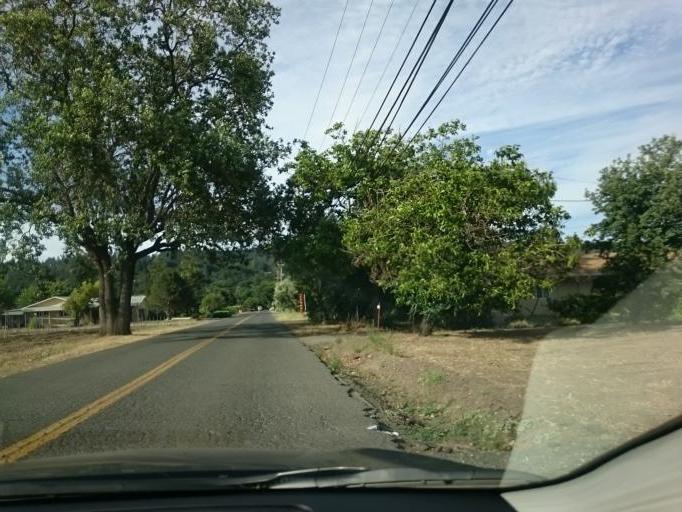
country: US
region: California
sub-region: Napa County
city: Saint Helena
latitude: 38.5141
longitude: -122.4745
